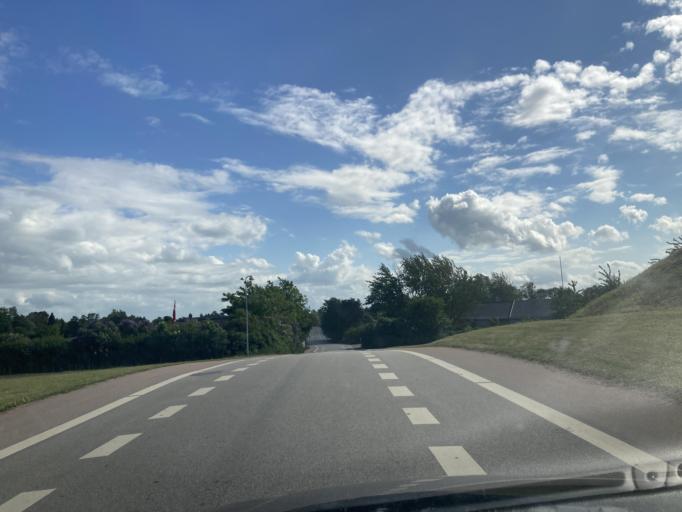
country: DK
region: Capital Region
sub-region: Gribskov Kommune
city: Helsinge
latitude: 56.0096
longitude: 12.1115
